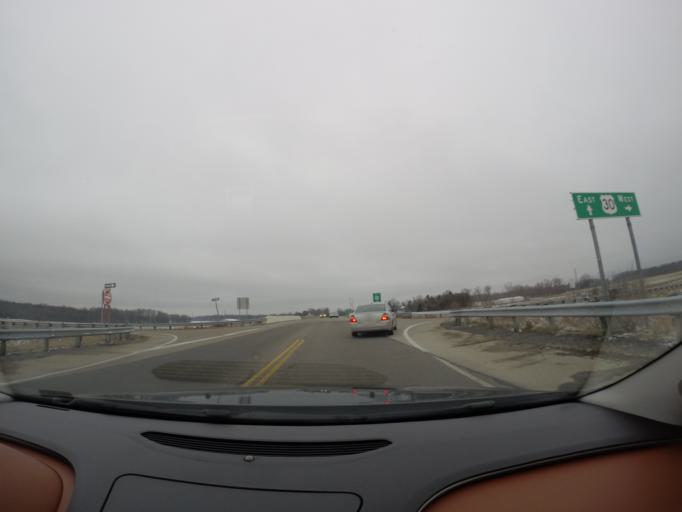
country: US
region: Ohio
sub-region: Wayne County
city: Smithville
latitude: 40.8107
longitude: -81.8441
